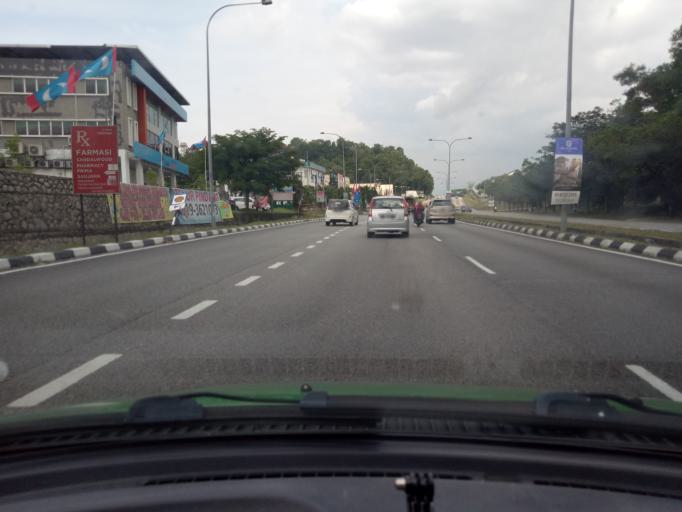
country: MY
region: Selangor
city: Kampong Baharu Balakong
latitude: 3.0069
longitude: 101.8044
